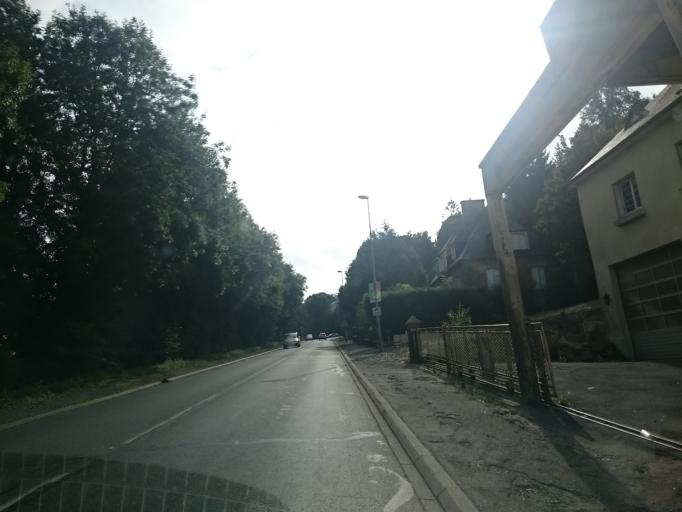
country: FR
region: Lower Normandy
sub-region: Departement de la Manche
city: Avranches
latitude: 48.6899
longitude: -1.3620
